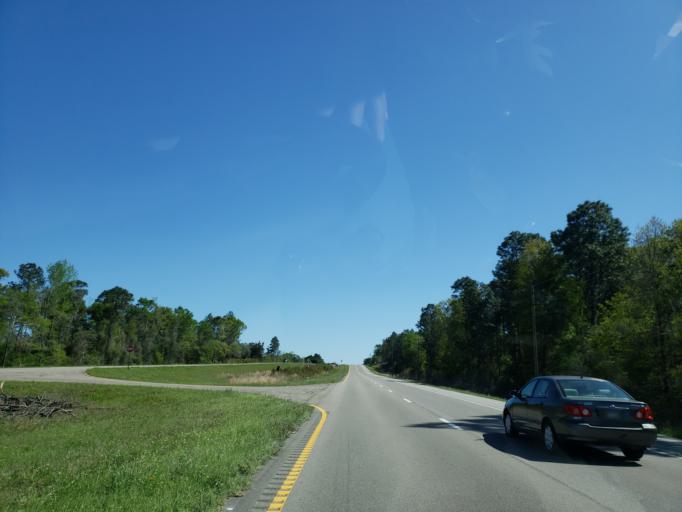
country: US
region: Mississippi
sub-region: Stone County
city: Wiggins
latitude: 30.9251
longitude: -89.1773
